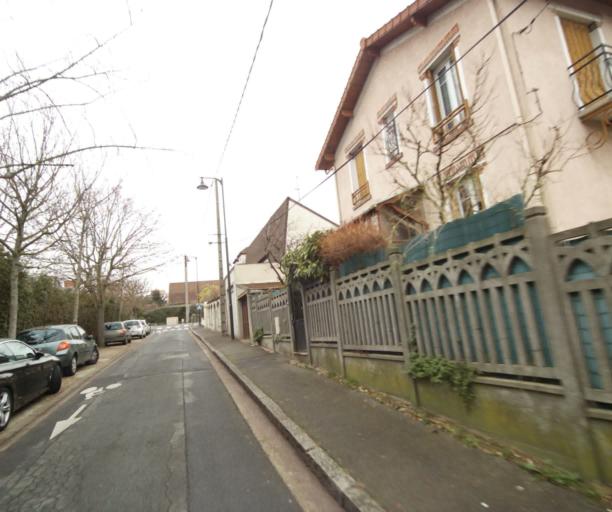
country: FR
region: Ile-de-France
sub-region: Departement des Hauts-de-Seine
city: Rueil-Malmaison
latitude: 48.8797
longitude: 2.1942
